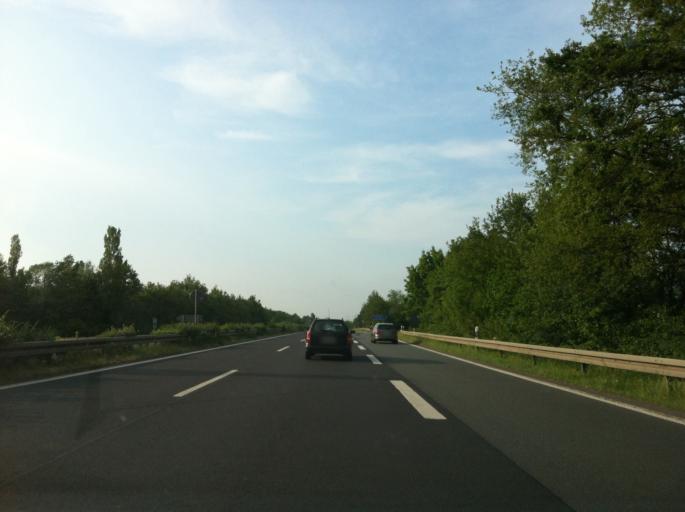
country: DE
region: Bavaria
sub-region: Regierungsbezirk Unterfranken
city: Kleinostheim
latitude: 49.9859
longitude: 9.0515
